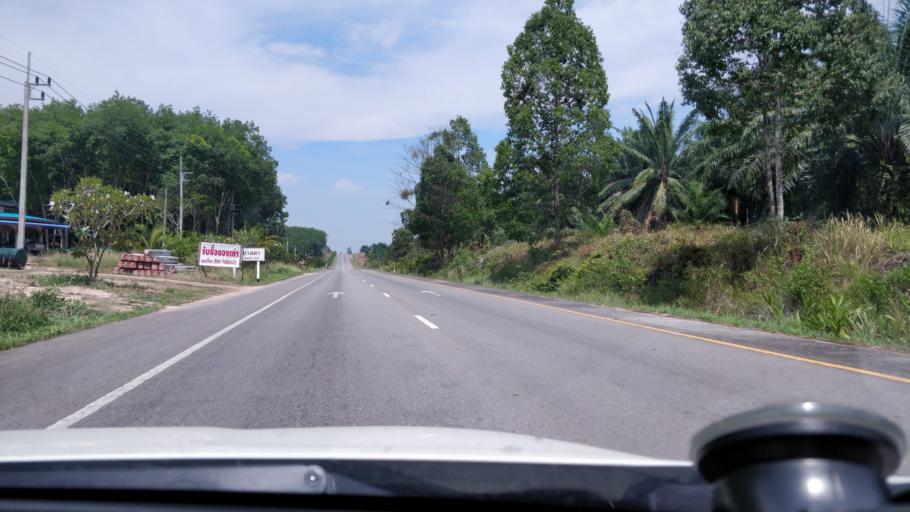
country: TH
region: Surat Thani
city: Chai Buri
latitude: 8.6420
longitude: 99.0569
